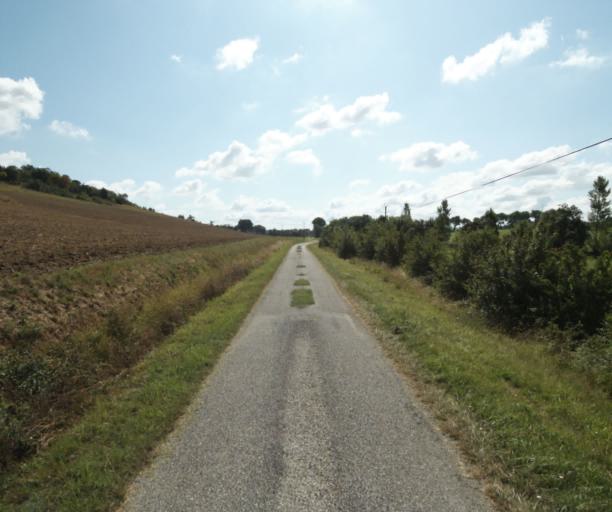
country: FR
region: Midi-Pyrenees
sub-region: Departement de la Haute-Garonne
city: Avignonet-Lauragais
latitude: 43.4476
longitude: 1.7864
